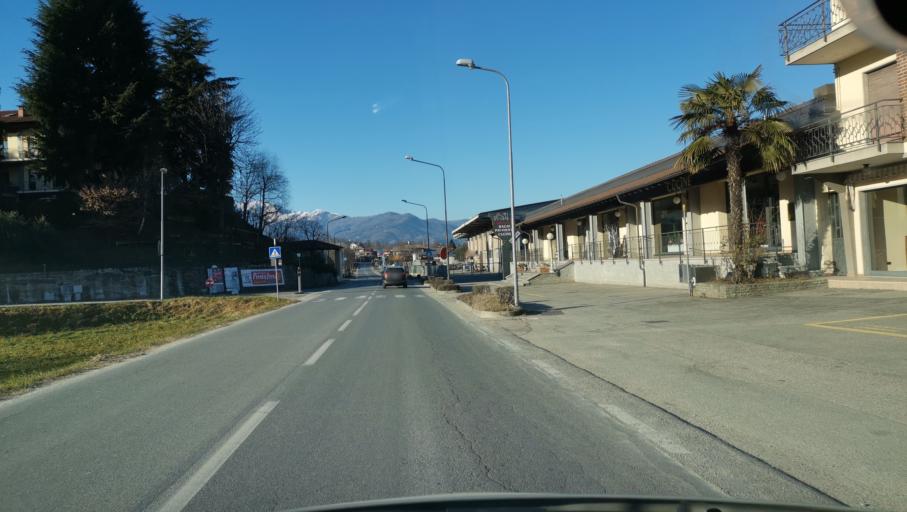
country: IT
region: Piedmont
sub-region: Provincia di Cuneo
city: Bagnolo Piemonte
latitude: 44.7649
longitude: 7.3120
